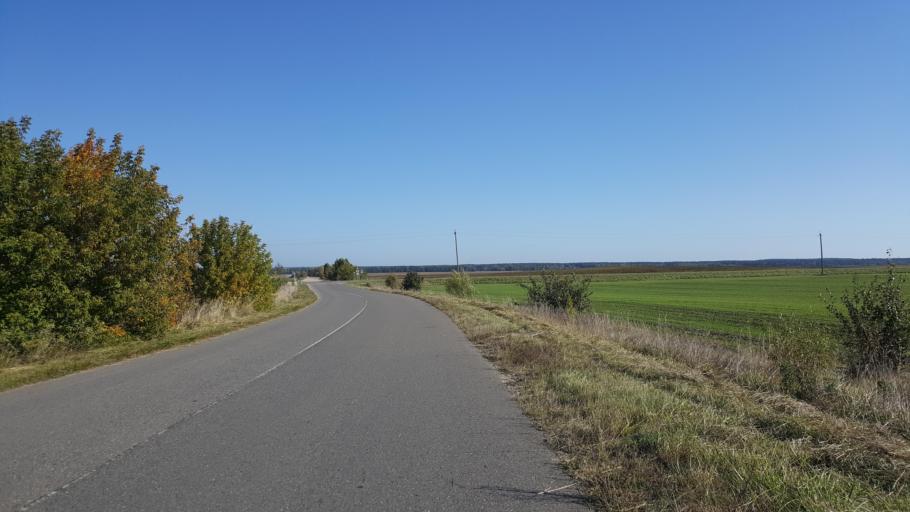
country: BY
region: Brest
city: Kamyanyets
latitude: 52.4105
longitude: 23.8516
